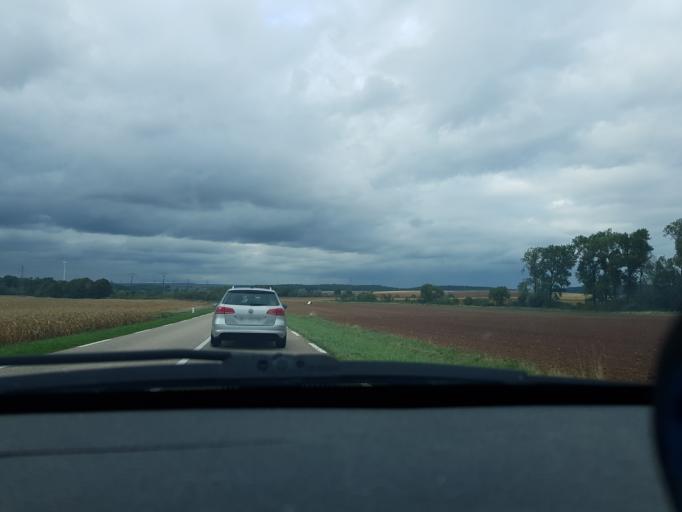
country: FR
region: Lorraine
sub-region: Departement de la Moselle
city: Morhange
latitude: 48.9460
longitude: 6.6108
